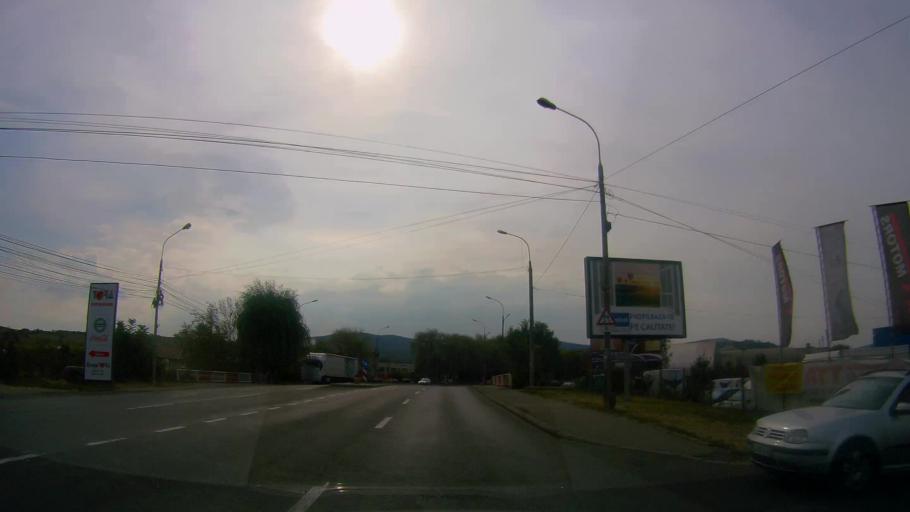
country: RO
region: Salaj
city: Zalau
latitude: 47.1979
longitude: 23.0590
